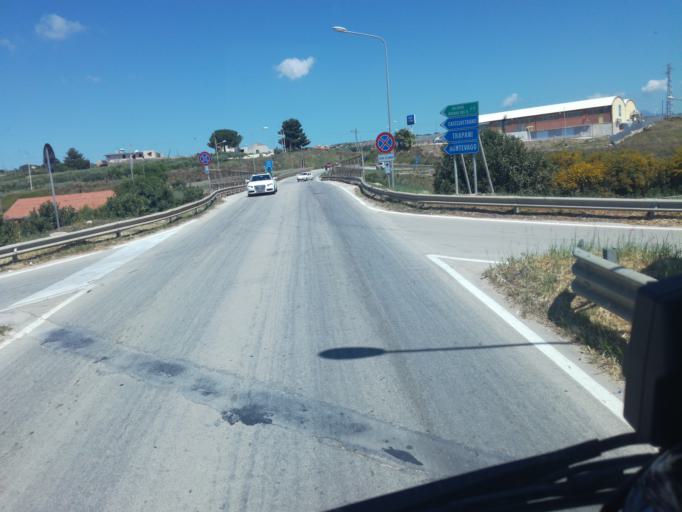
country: IT
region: Sicily
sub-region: Agrigento
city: Menfi
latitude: 37.6162
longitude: 12.9744
